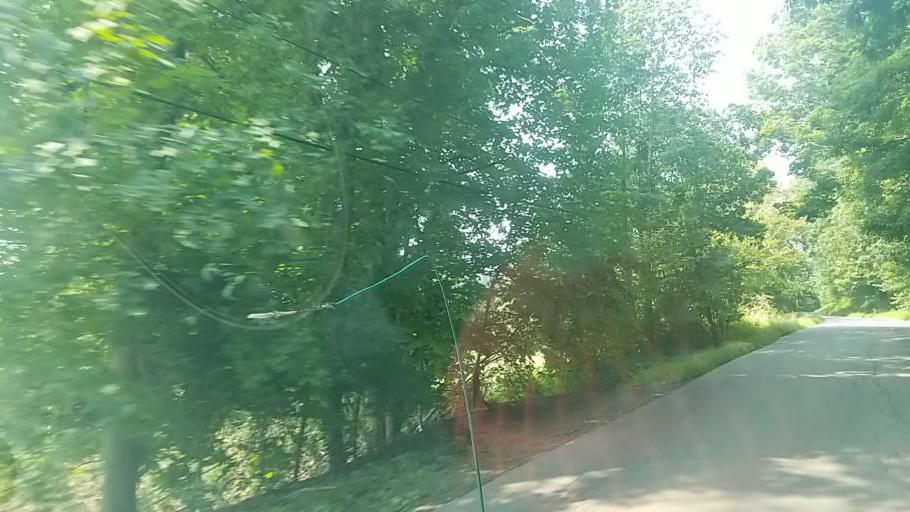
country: US
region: New York
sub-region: Montgomery County
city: Fonda
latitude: 42.9490
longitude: -74.4422
